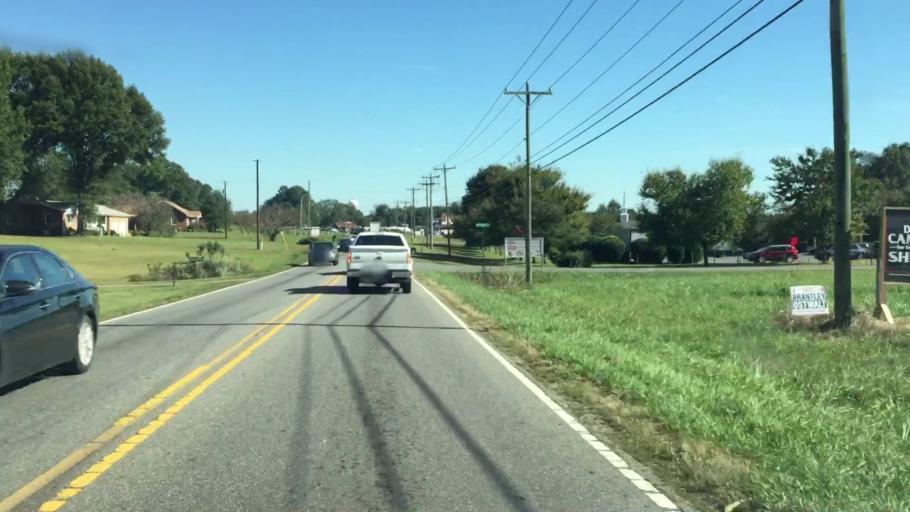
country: US
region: North Carolina
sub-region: Catawba County
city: Lake Norman of Catawba
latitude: 35.5977
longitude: -80.8855
